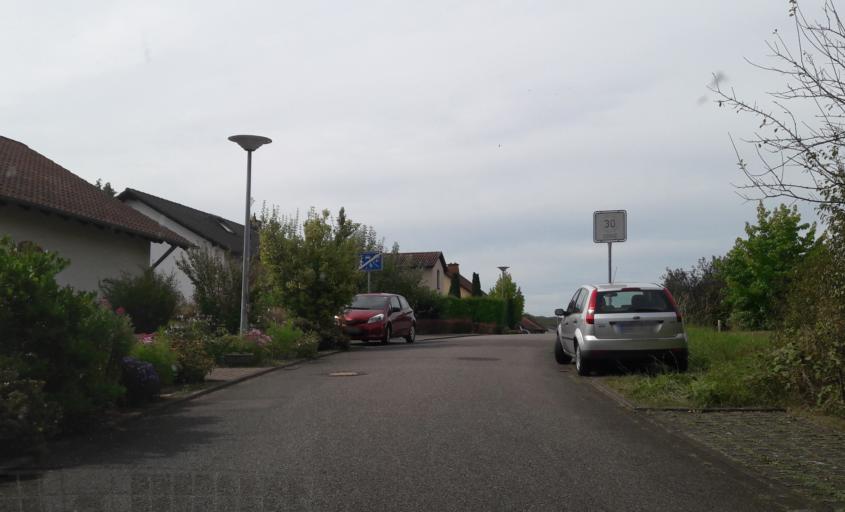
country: DE
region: Saarland
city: Oberthal
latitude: 49.4928
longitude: 7.1080
